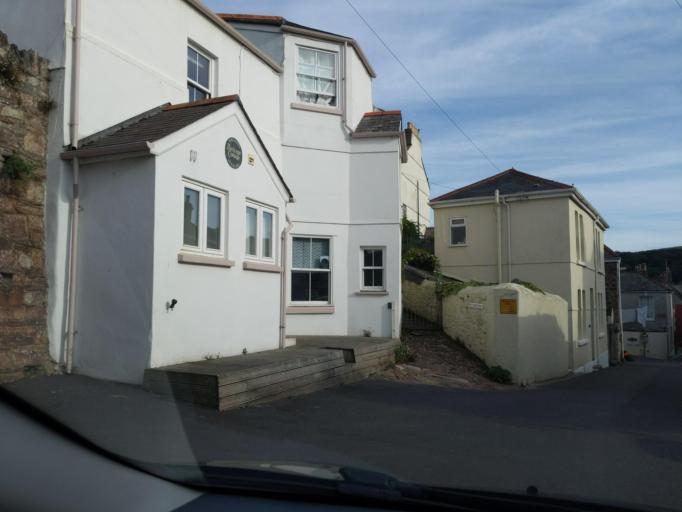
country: GB
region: England
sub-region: Cornwall
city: Millbrook
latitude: 50.3349
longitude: -4.2017
